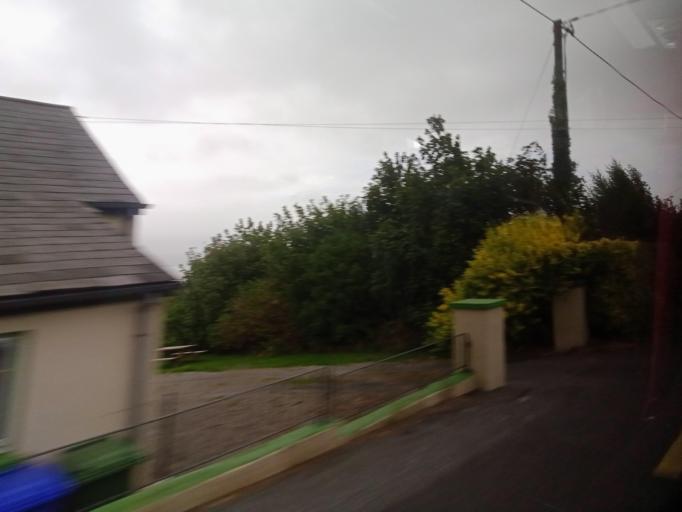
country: IE
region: Munster
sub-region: Waterford
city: Dungarvan
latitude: 52.0498
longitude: -7.6175
